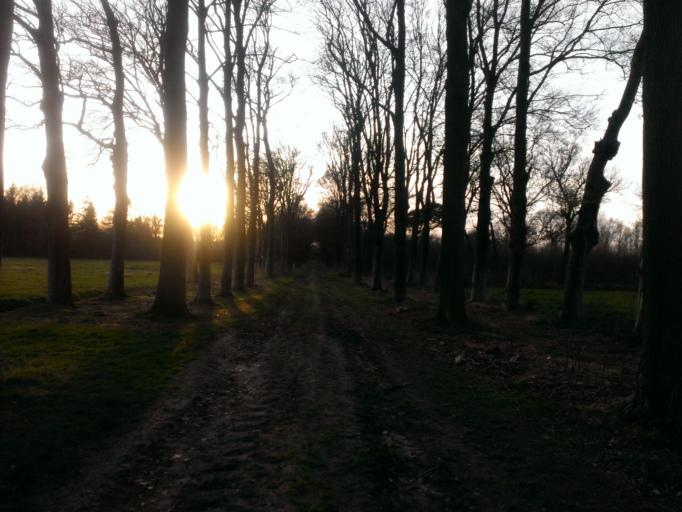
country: NL
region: Gelderland
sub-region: Gemeente Heerde
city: Heerde
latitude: 52.3950
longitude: 6.0527
